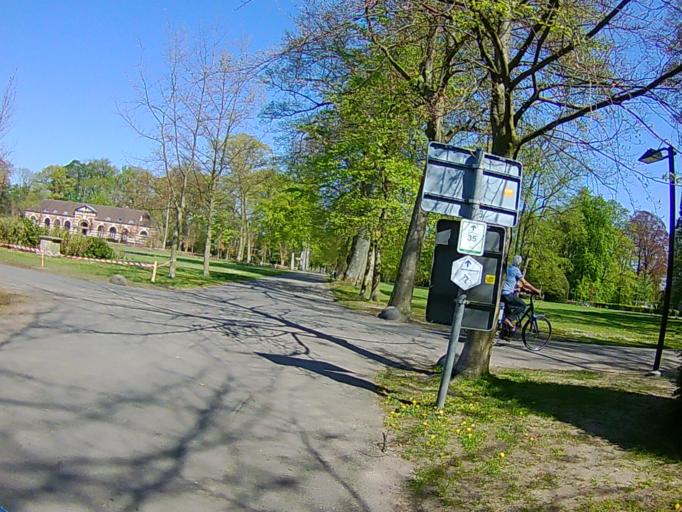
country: BE
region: Flanders
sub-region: Provincie Antwerpen
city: Brasschaat
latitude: 51.2878
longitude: 4.4966
